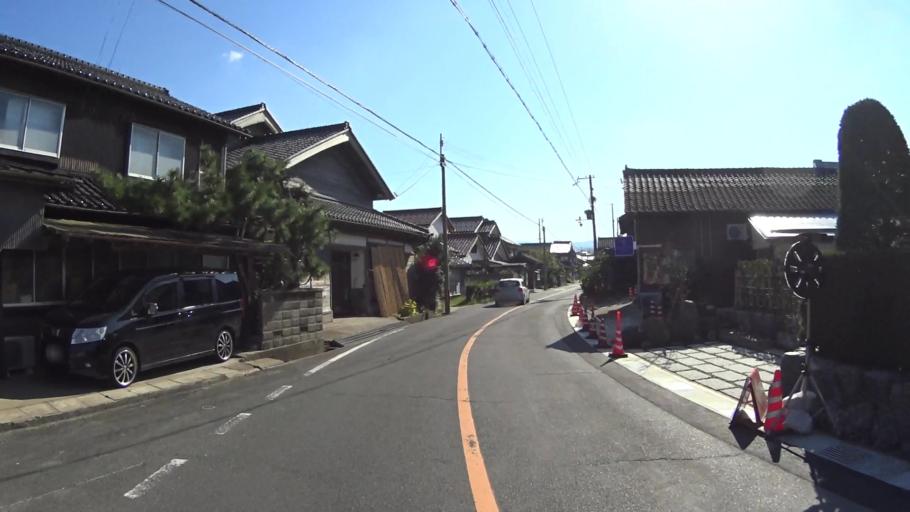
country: JP
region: Kyoto
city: Miyazu
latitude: 35.6895
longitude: 135.0349
